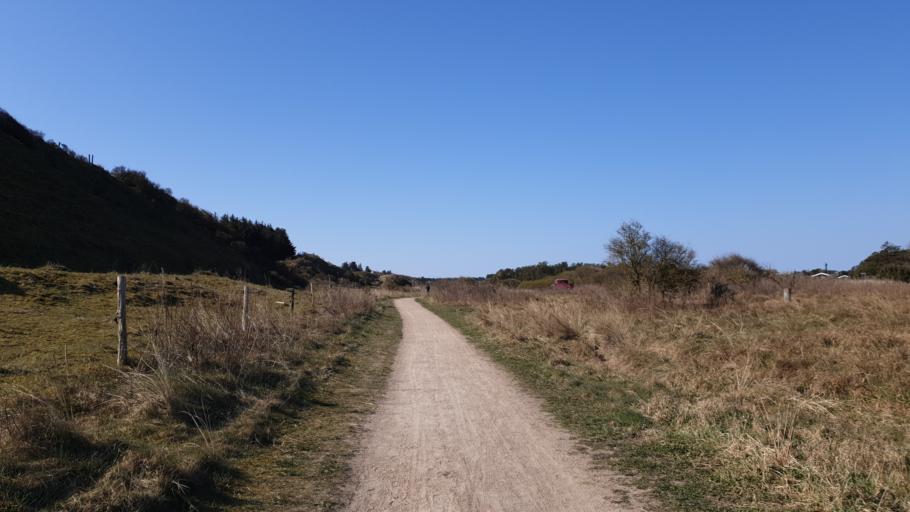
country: DK
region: North Denmark
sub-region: Hjorring Kommune
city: Hjorring
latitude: 57.4950
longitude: 9.8479
